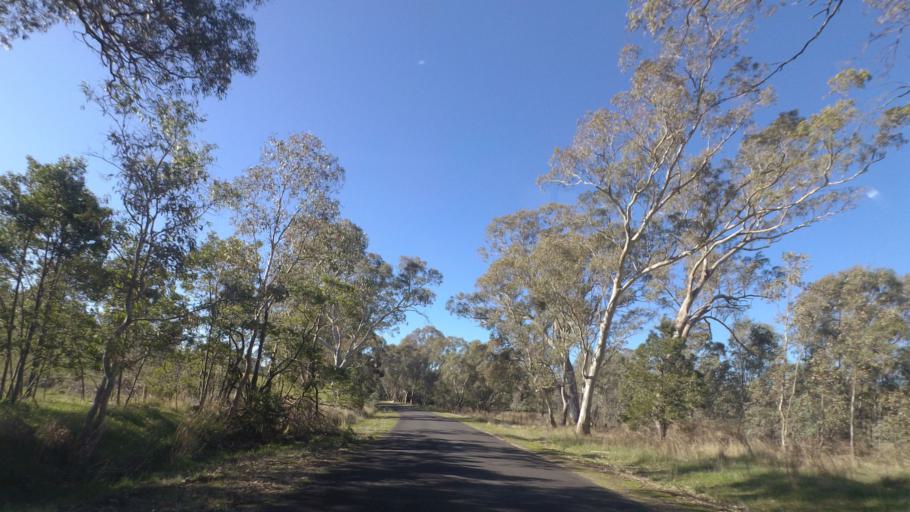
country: AU
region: Victoria
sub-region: Mount Alexander
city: Castlemaine
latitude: -36.9681
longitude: 144.3216
